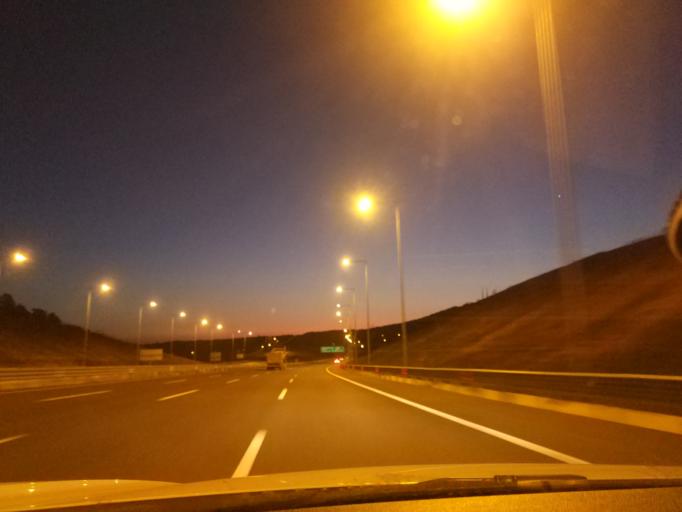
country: TR
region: Istanbul
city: Sancaktepe
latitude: 41.0487
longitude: 29.2670
